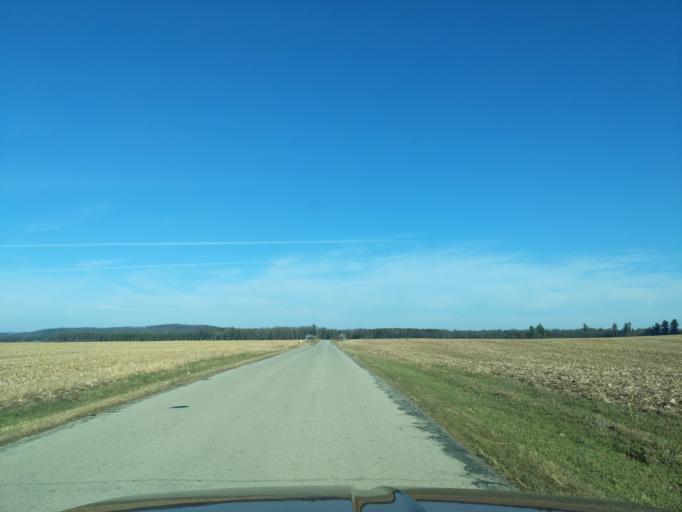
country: US
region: Wisconsin
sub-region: Waushara County
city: Silver Lake
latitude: 44.0912
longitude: -89.1739
